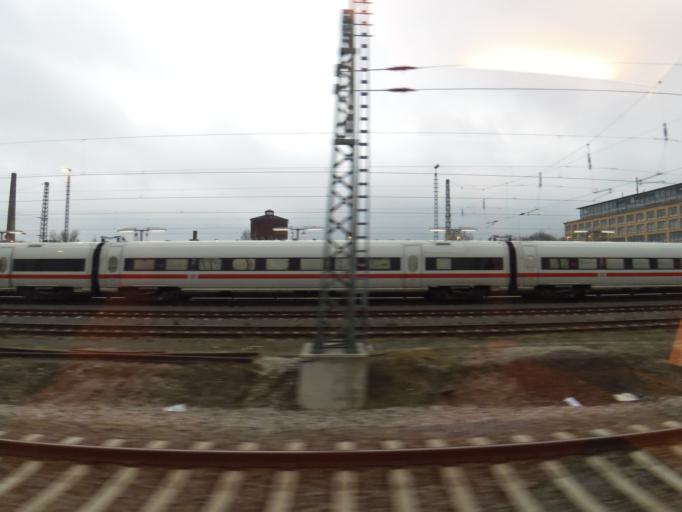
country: DE
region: Saxony
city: Leipzig
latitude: 51.3504
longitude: 12.4012
